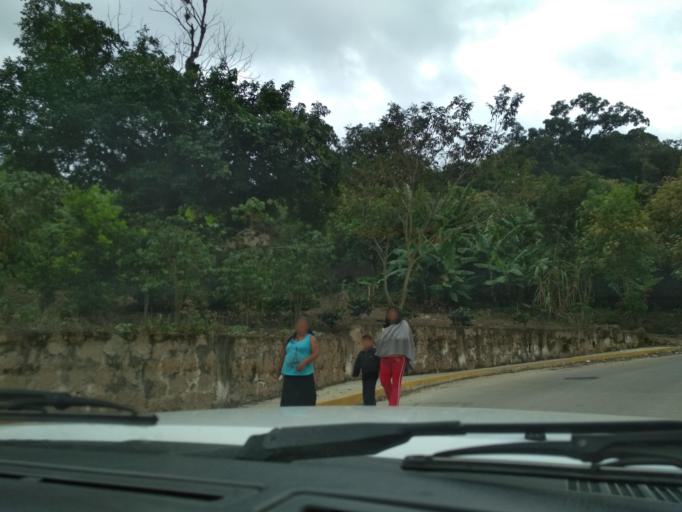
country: MX
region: Veracruz
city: El Castillo
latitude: 19.5812
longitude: -96.8678
